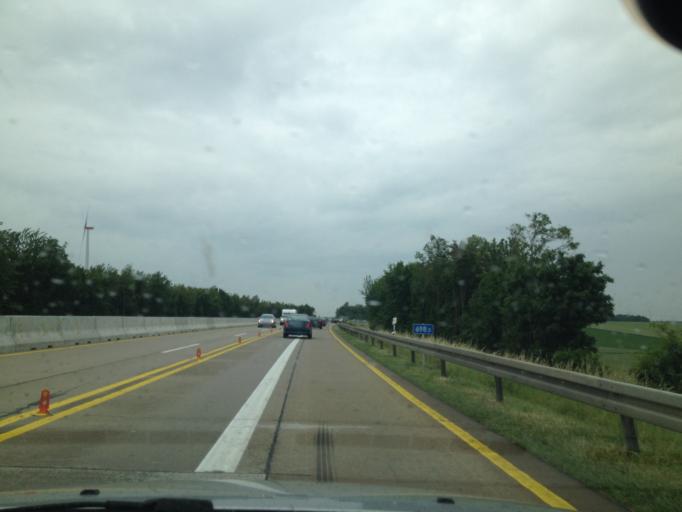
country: DE
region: Bavaria
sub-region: Regierungsbezirk Mittelfranken
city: Simmershofen
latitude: 49.5456
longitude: 10.1651
